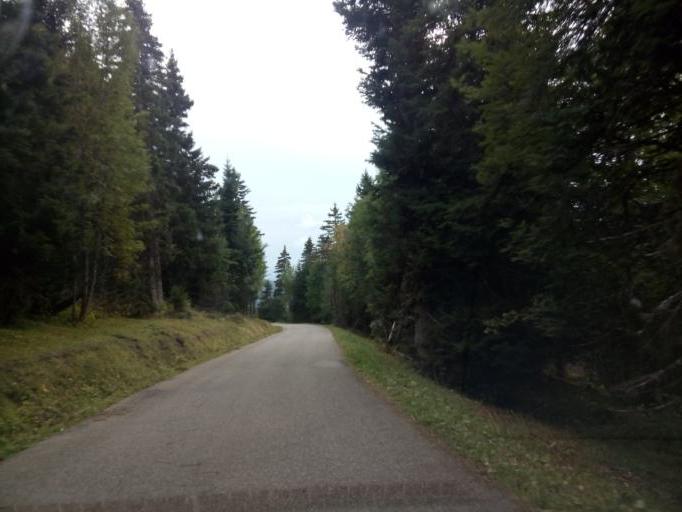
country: FR
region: Rhone-Alpes
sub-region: Departement de l'Isere
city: Vaulnaveys-le-Bas
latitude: 45.0413
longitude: 5.8644
